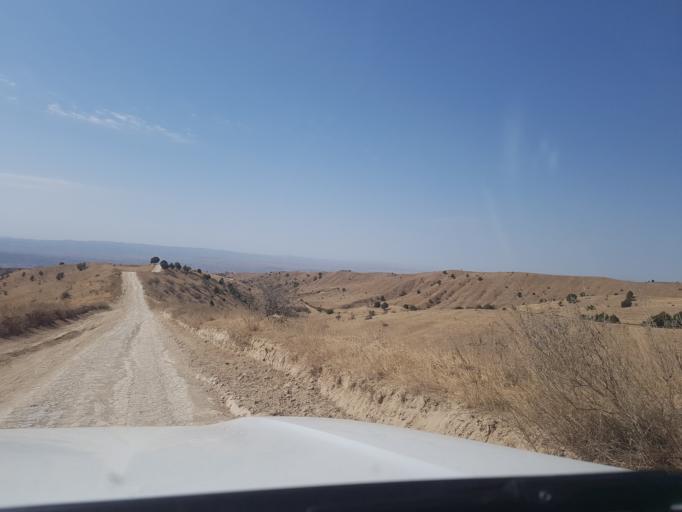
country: TM
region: Ahal
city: Baharly
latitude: 38.3019
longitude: 56.9440
